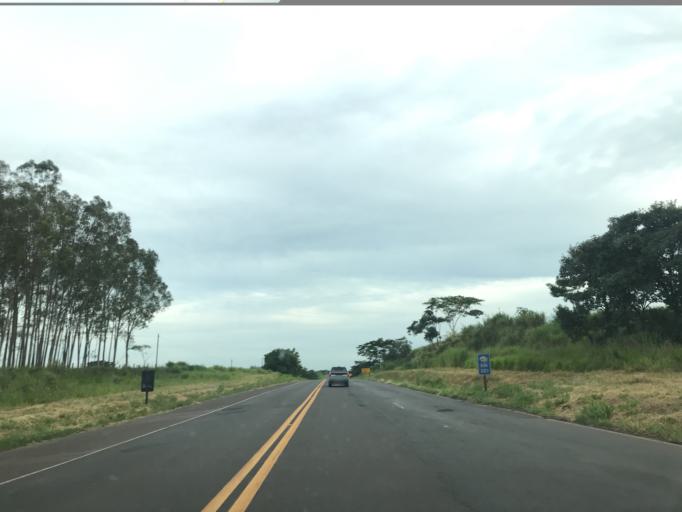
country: BR
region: Sao Paulo
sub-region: Tupa
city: Tupa
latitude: -21.6046
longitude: -50.4709
